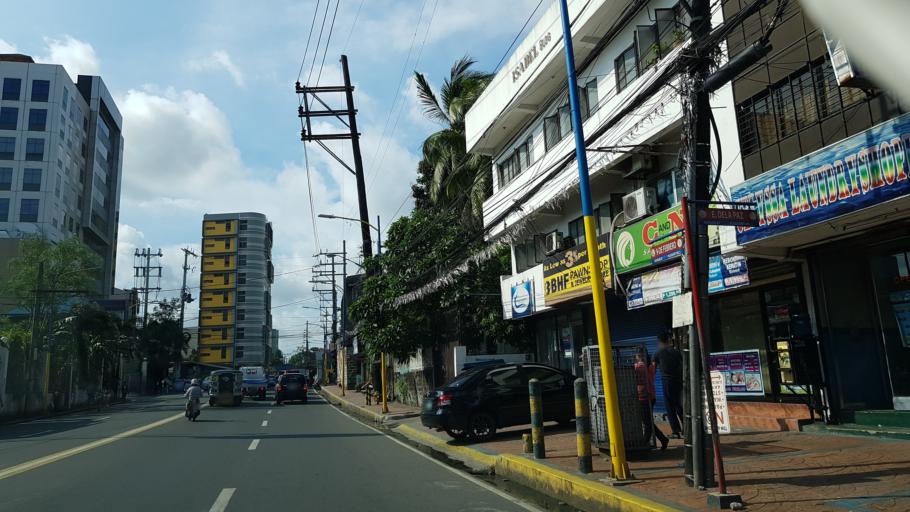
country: PH
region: Metro Manila
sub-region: Mandaluyong
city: Mandaluyong City
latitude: 14.5881
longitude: 121.0377
